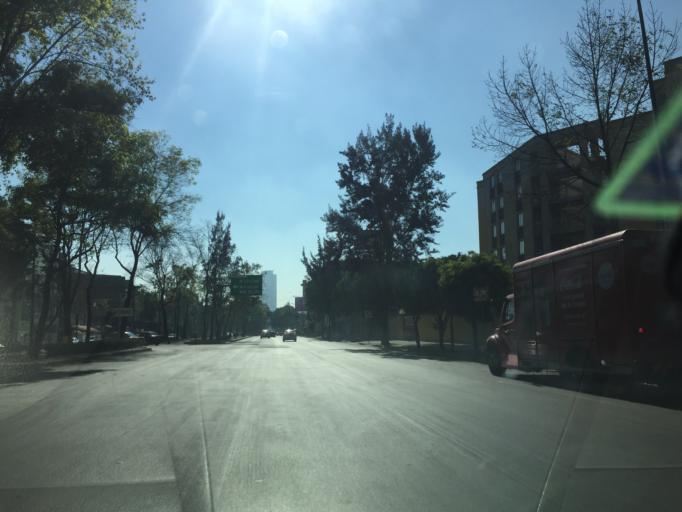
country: MX
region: Mexico City
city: Miguel Hidalgo
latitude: 19.4535
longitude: -99.1869
